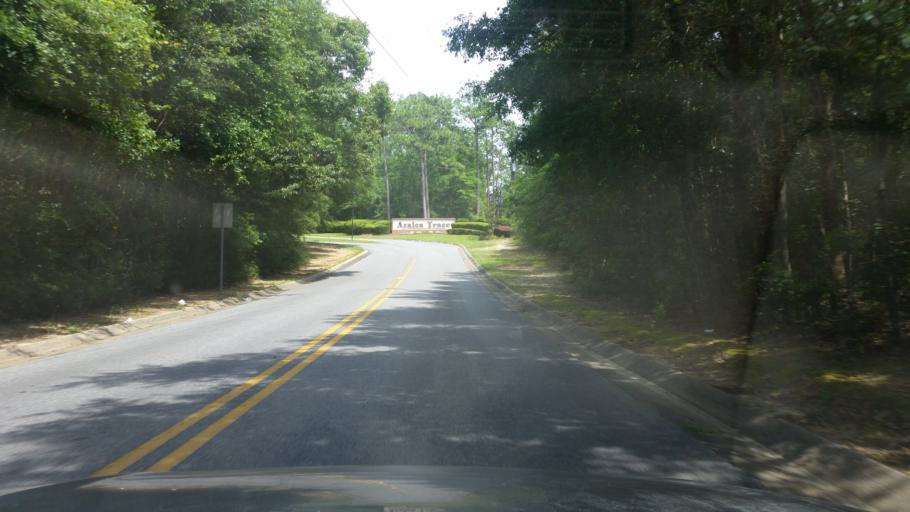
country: US
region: Florida
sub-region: Escambia County
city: Ferry Pass
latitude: 30.5393
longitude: -87.2120
